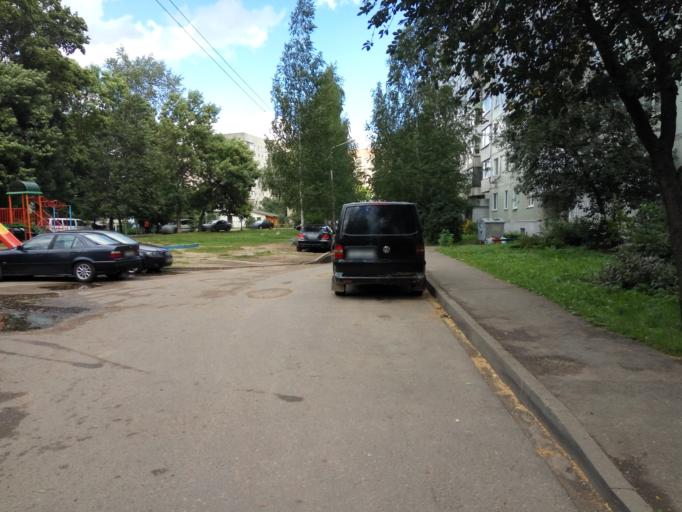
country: BY
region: Vitebsk
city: Vitebsk
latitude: 55.1915
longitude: 30.2451
